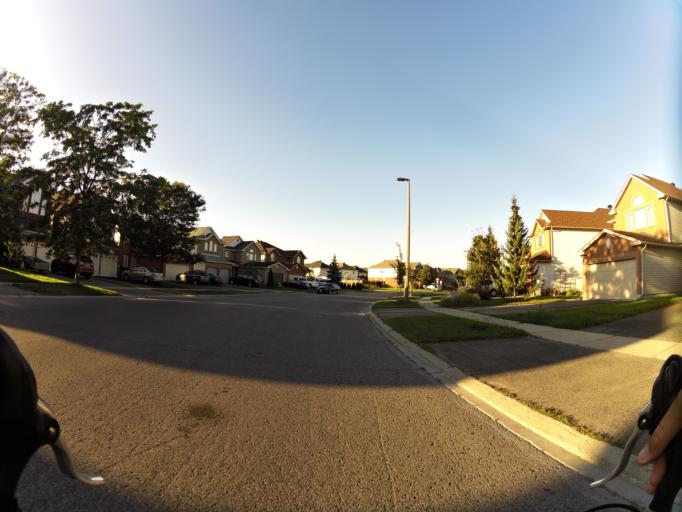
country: CA
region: Ontario
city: Bells Corners
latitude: 45.3554
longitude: -75.9227
